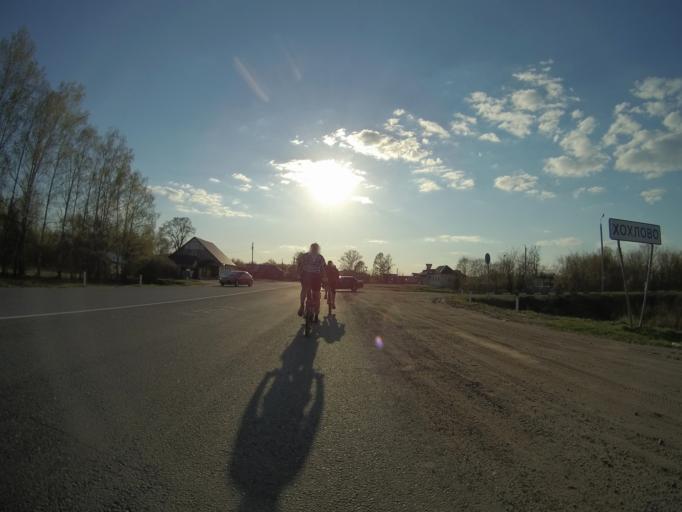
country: RU
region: Vladimir
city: Orgtrud
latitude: 56.2031
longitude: 40.7590
